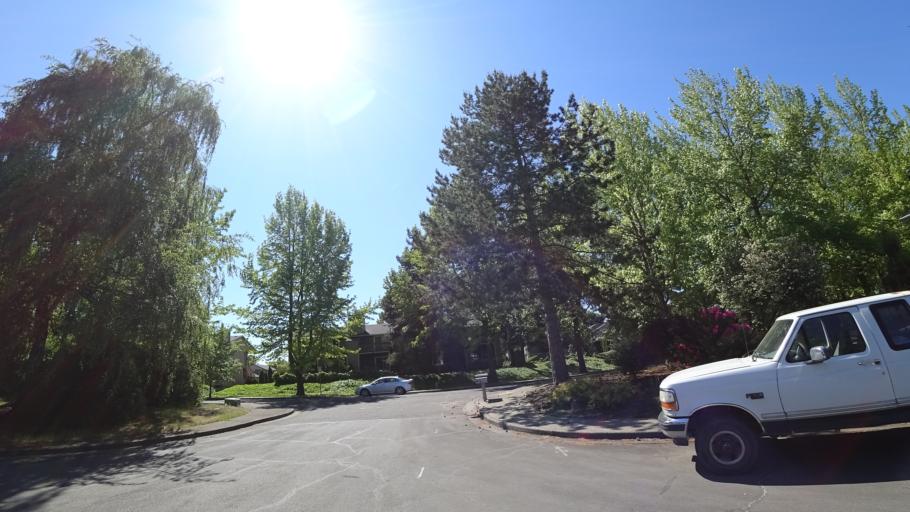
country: US
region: Oregon
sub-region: Washington County
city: Tigard
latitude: 45.4485
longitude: -122.8008
